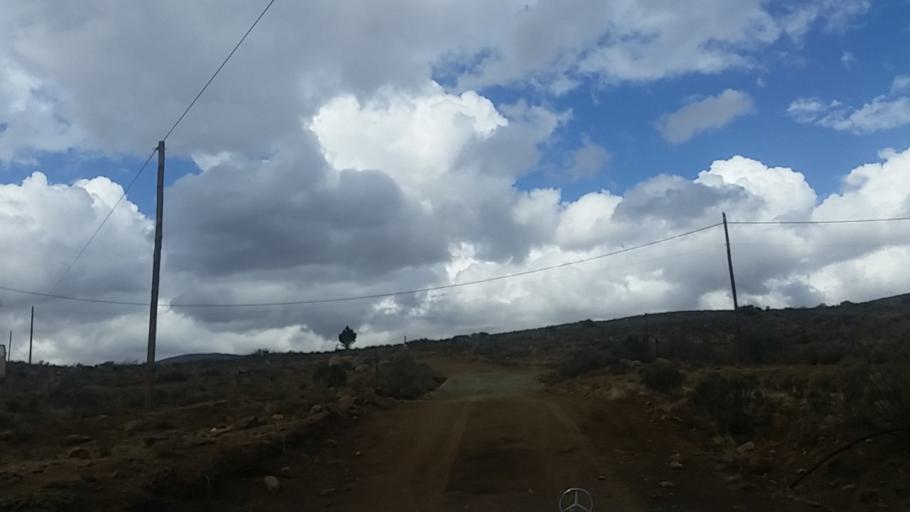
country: ZA
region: Eastern Cape
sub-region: Chris Hani District Municipality
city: Middelburg
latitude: -31.7918
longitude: 24.6603
